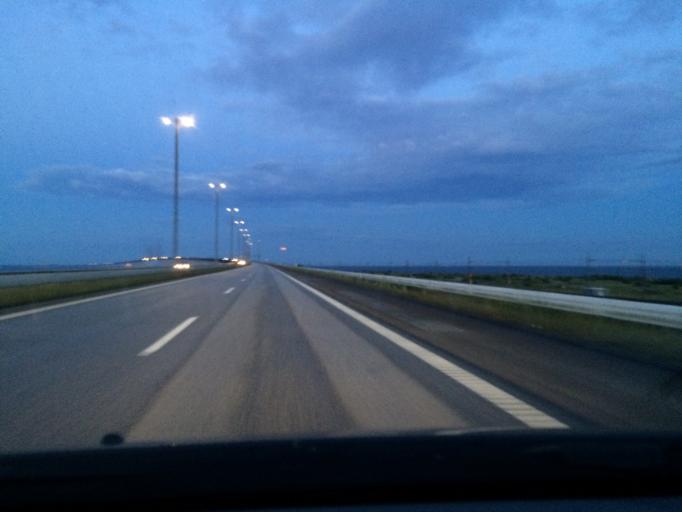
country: DK
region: Capital Region
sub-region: Dragor Kommune
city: Dragor
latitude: 55.5959
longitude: 12.7603
